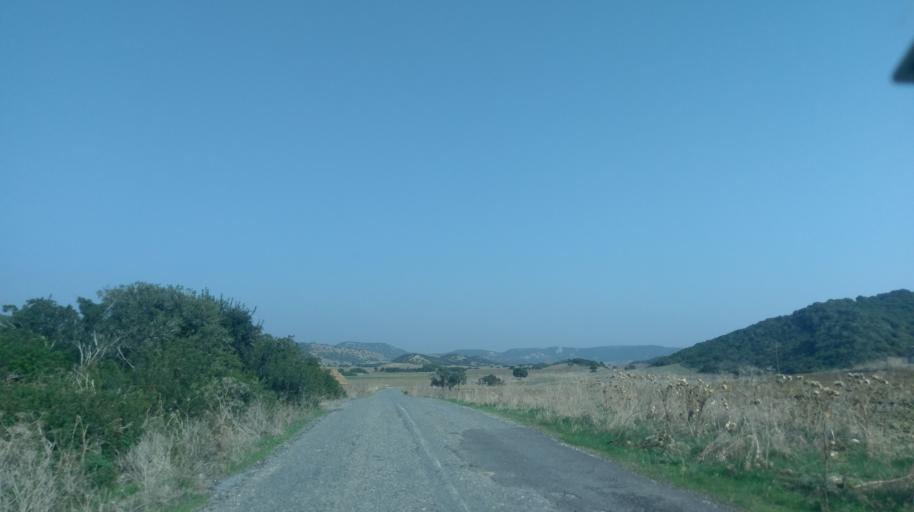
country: CY
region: Ammochostos
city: Rizokarpaso
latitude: 35.6368
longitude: 34.5107
